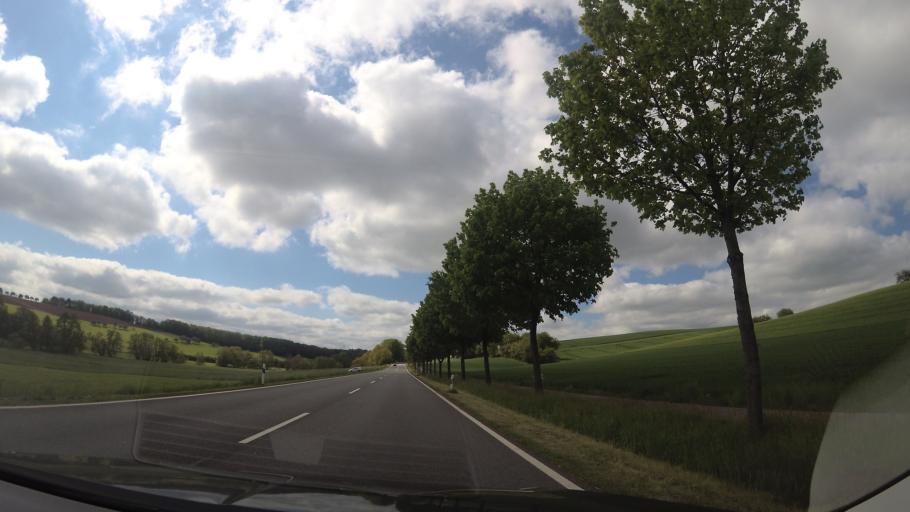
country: DE
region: Saarland
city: Lebach
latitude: 49.4223
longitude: 6.9406
